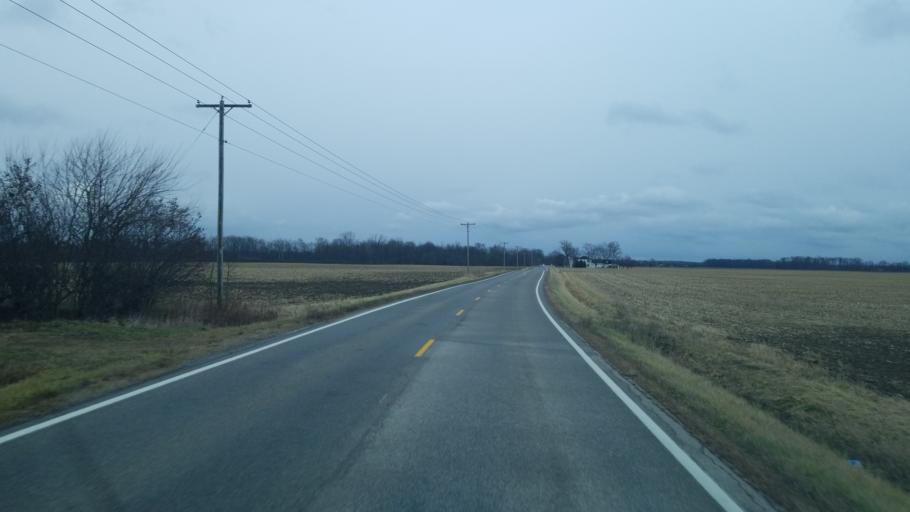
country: US
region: Ohio
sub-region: Union County
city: Richwood
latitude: 40.3372
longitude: -83.2285
